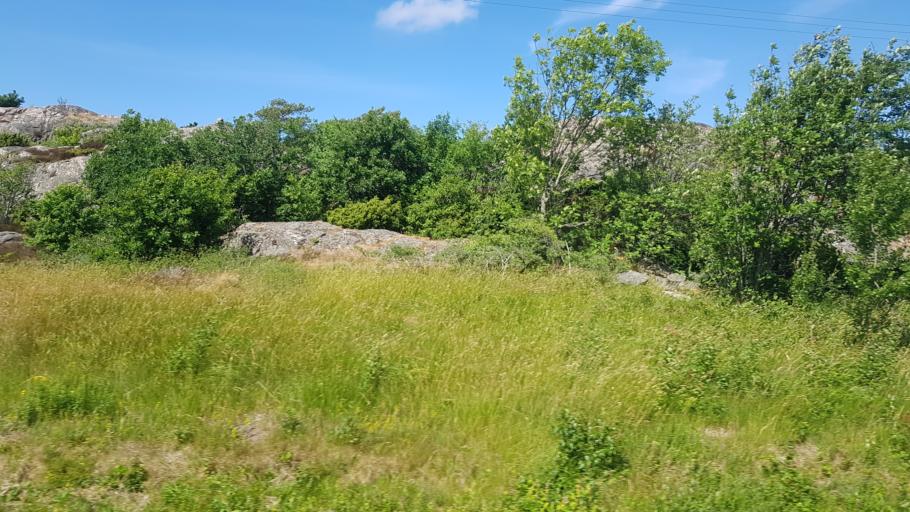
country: SE
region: Vaestra Goetaland
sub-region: Tjorns Kommun
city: Skaerhamn
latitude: 57.9717
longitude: 11.5580
